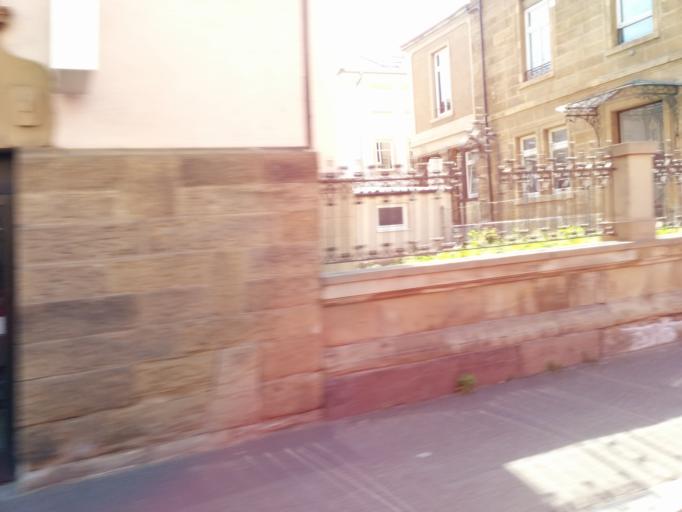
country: DE
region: Baden-Wuerttemberg
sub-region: Regierungsbezirk Stuttgart
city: Heilbronn
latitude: 49.1373
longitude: 9.2194
